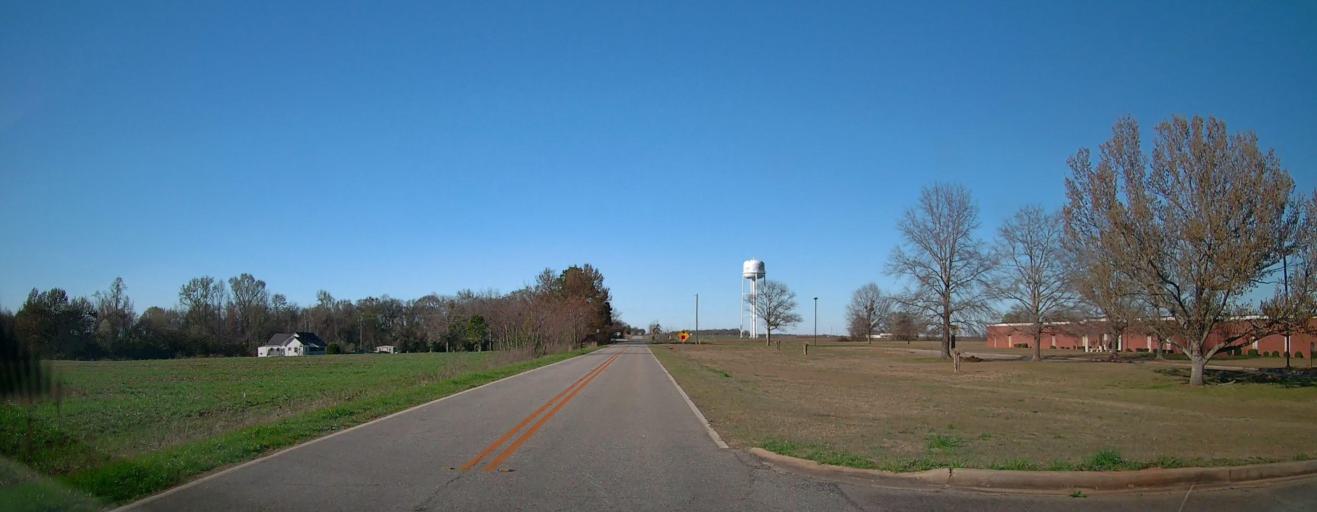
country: US
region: Georgia
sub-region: Peach County
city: Fort Valley
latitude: 32.5684
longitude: -83.9158
